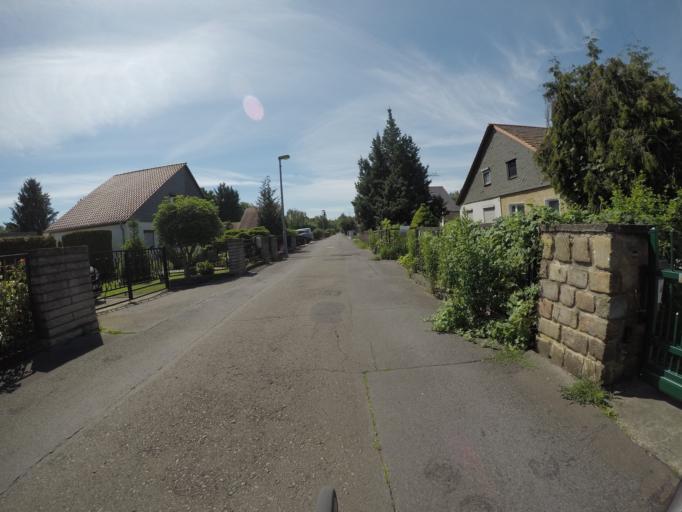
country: DE
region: Berlin
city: Biesdorf
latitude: 52.5046
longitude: 13.5428
